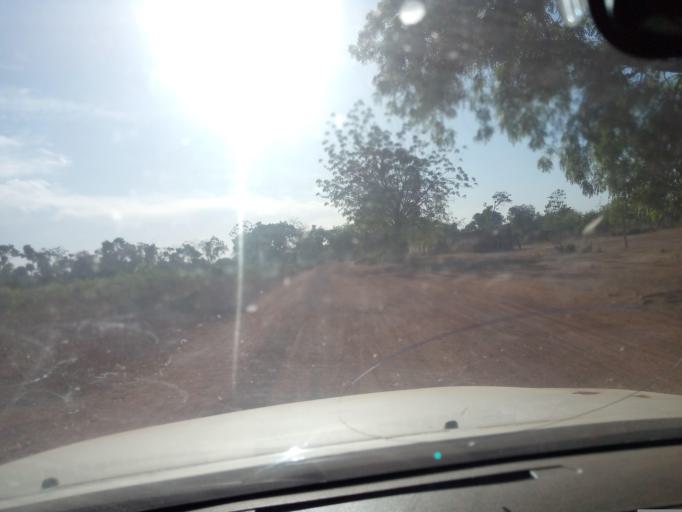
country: ML
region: Sikasso
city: Sikasso
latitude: 11.4844
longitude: -5.4863
